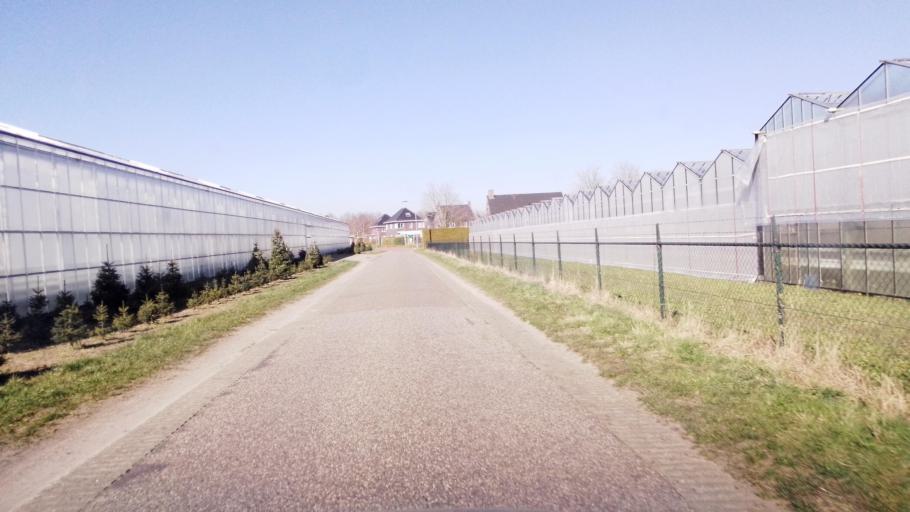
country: NL
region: Limburg
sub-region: Gemeente Peel en Maas
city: Maasbree
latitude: 51.4443
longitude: 6.0452
